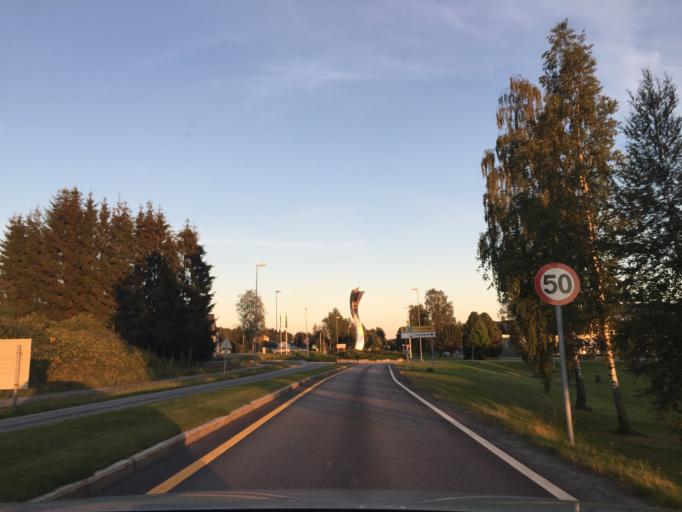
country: NO
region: Hedmark
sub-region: Kongsvinger
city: Kongsvinger
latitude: 60.2027
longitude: 11.9772
